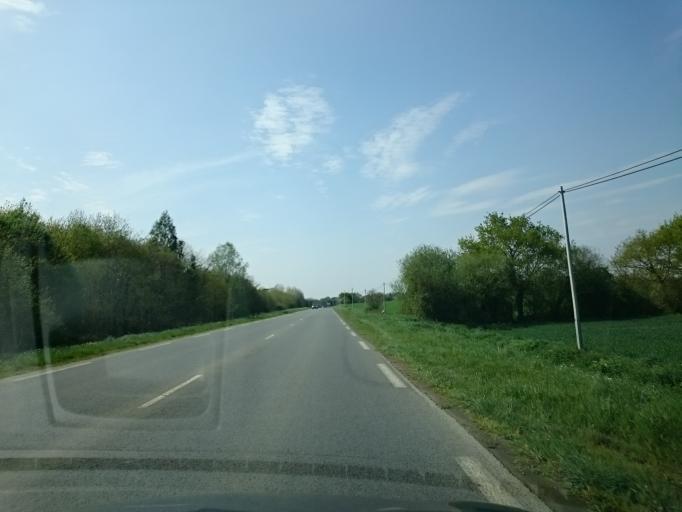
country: FR
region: Brittany
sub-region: Departement d'Ille-et-Vilaine
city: Chantepie
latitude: 48.0773
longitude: -1.5908
